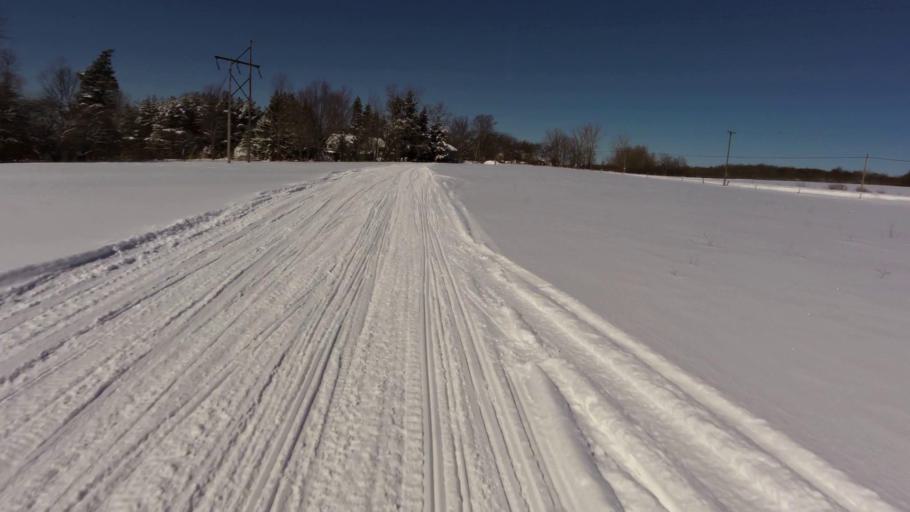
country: US
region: New York
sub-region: Chautauqua County
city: Mayville
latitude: 42.2608
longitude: -79.4502
